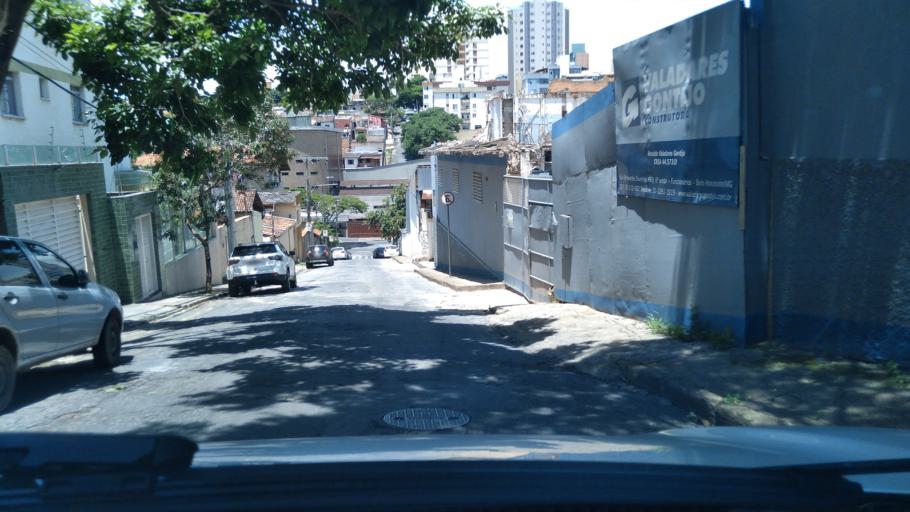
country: BR
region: Minas Gerais
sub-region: Contagem
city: Contagem
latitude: -19.9290
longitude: -43.9962
